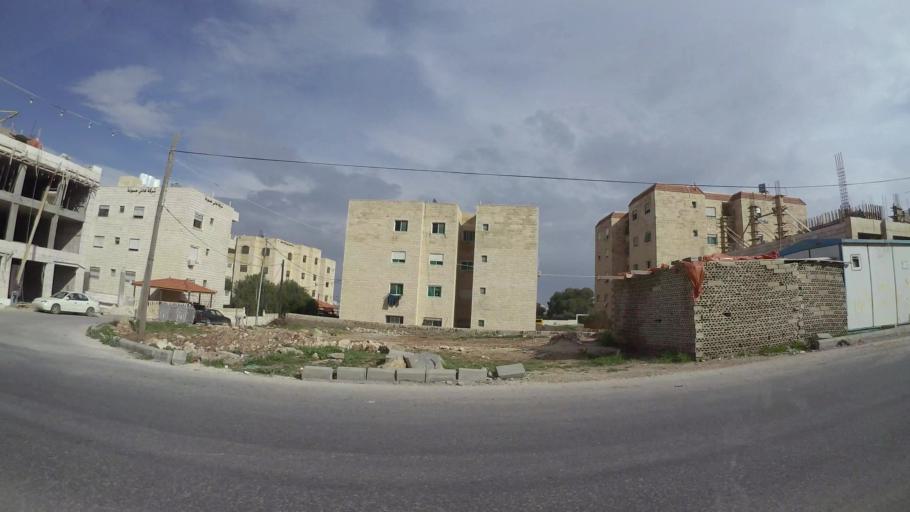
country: JO
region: Amman
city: Amman
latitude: 32.0094
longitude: 35.9521
